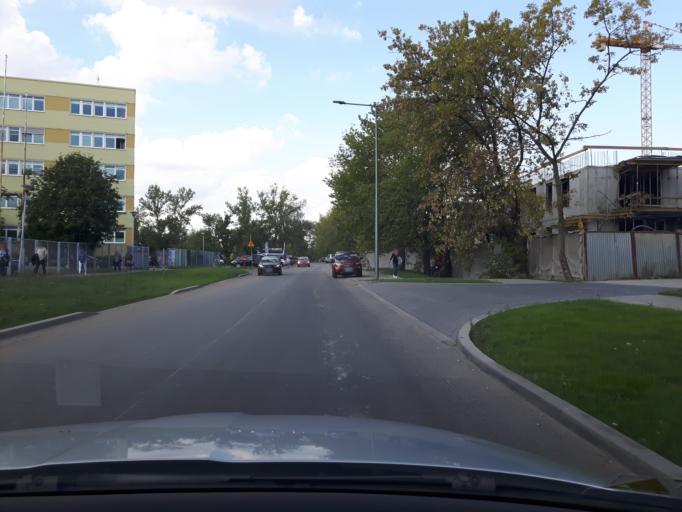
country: PL
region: Masovian Voivodeship
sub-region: Warszawa
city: Praga Poludnie
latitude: 52.2529
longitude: 21.0742
